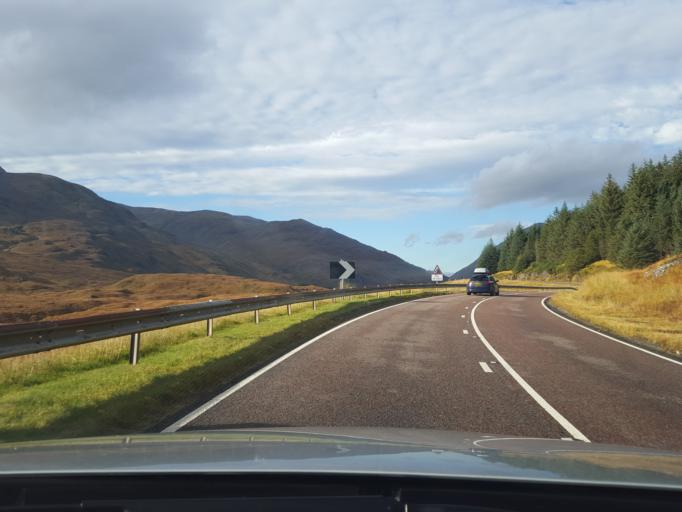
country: GB
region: Scotland
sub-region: Highland
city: Fort William
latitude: 57.1518
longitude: -5.2337
